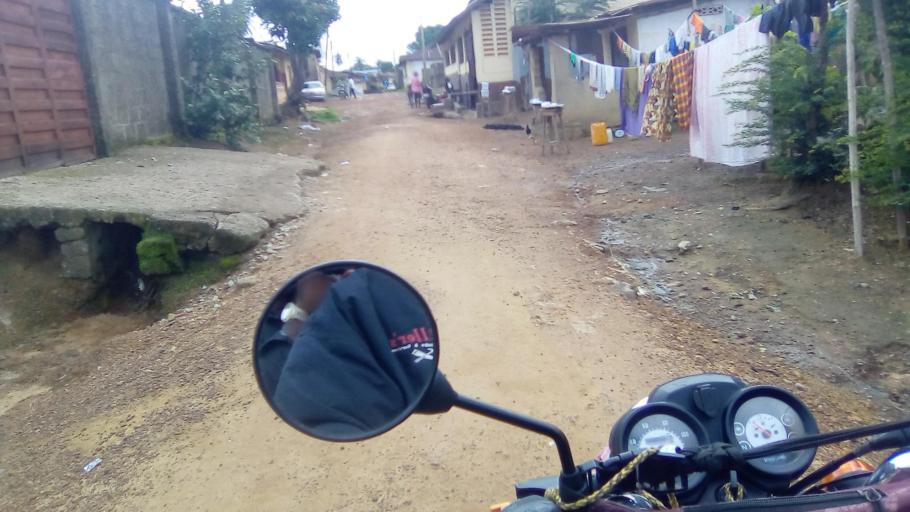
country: SL
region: Southern Province
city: Bo
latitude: 7.9568
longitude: -11.7501
